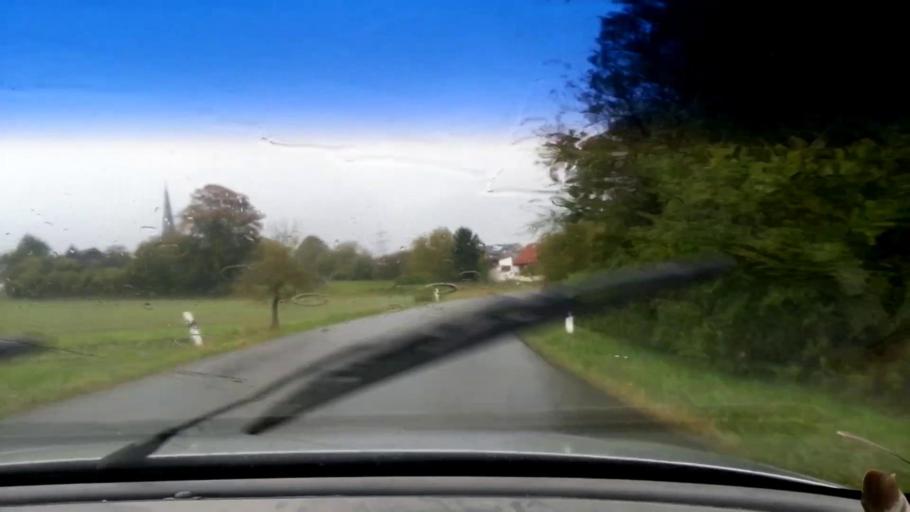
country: DE
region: Bavaria
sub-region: Upper Franconia
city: Wattendorf
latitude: 50.0522
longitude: 11.1429
